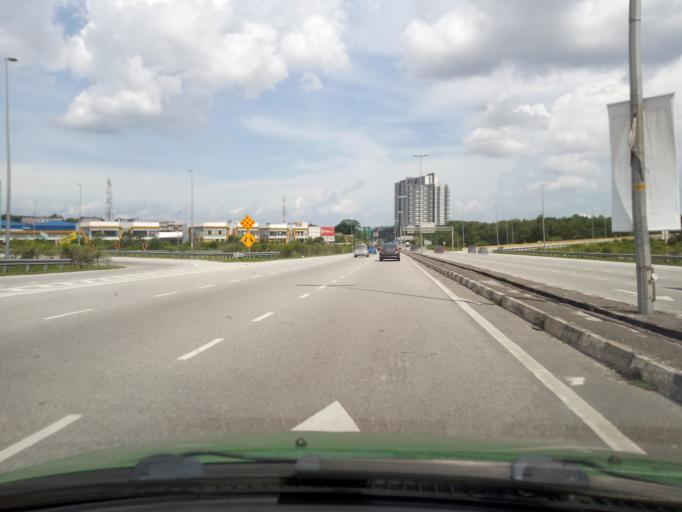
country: MY
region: Selangor
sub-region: Hulu Langat
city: Semenyih
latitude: 2.9700
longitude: 101.8338
